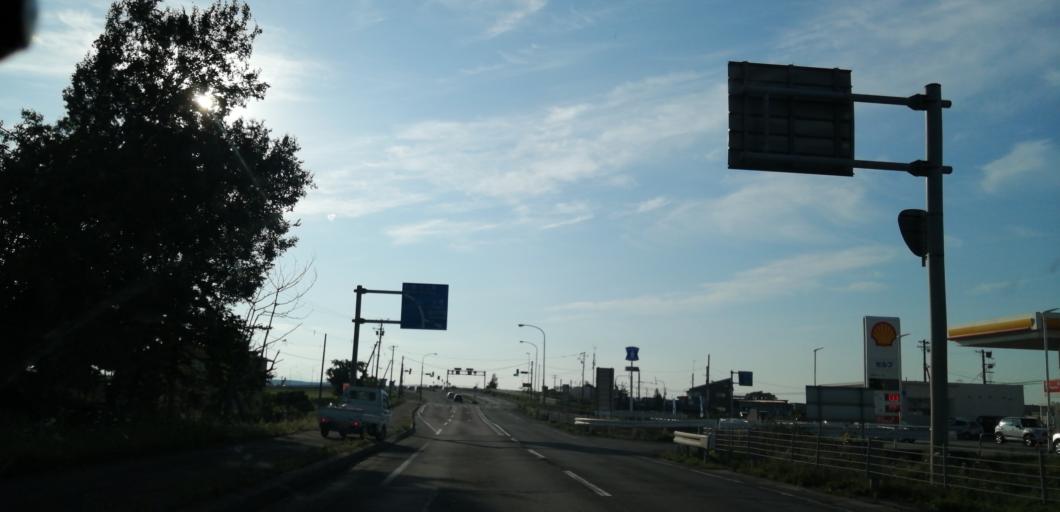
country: JP
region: Hokkaido
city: Kitahiroshima
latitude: 42.9963
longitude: 141.5907
